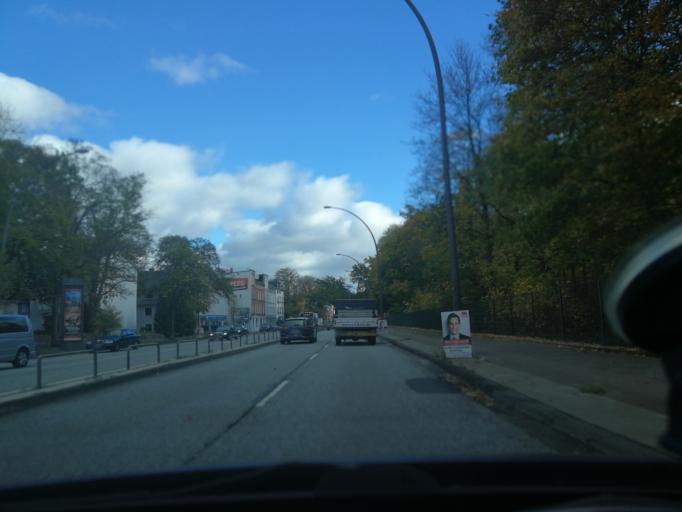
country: DE
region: Hamburg
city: Harburg
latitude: 53.4707
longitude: 9.9288
